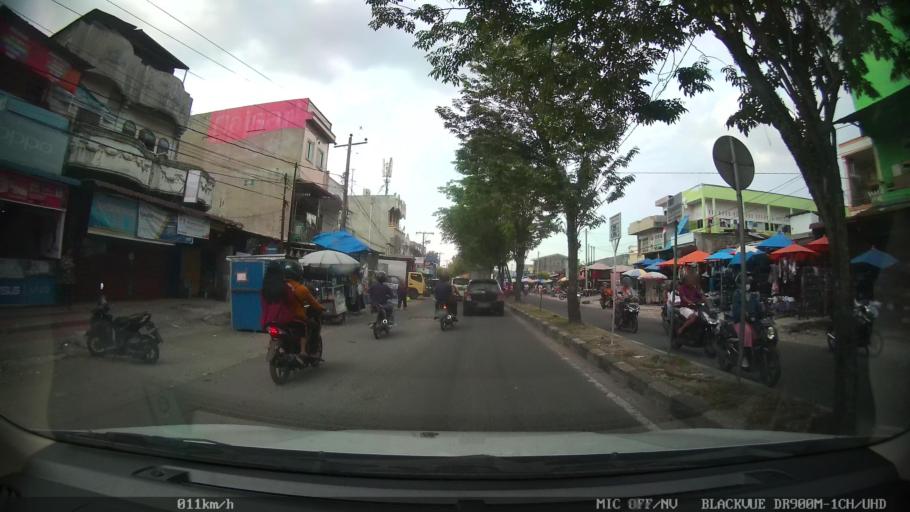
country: ID
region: North Sumatra
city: Sunggal
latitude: 3.5414
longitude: 98.6047
